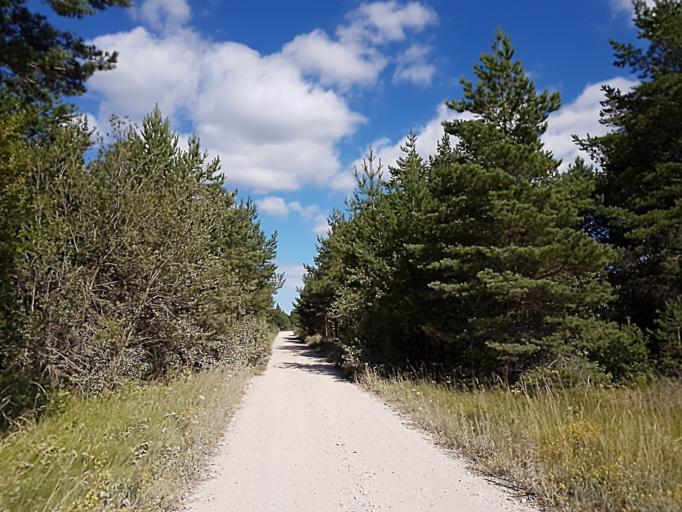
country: SE
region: Gotland
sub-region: Gotland
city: Visby
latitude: 57.6055
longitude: 18.3530
